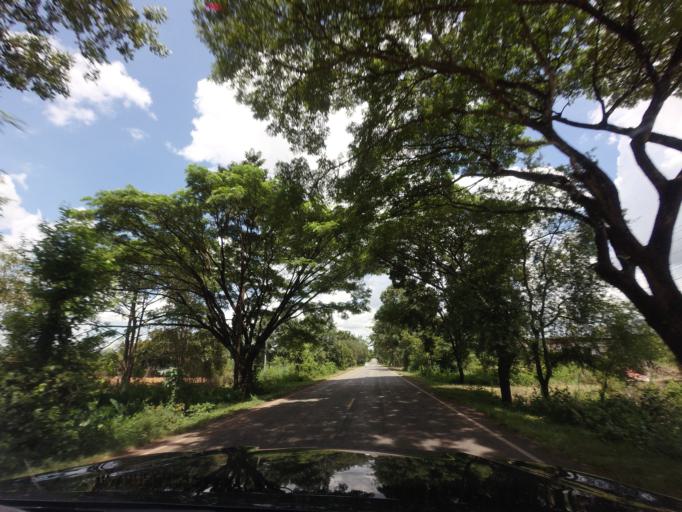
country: TH
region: Changwat Udon Thani
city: Phibun Rak
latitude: 17.5915
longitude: 103.0523
